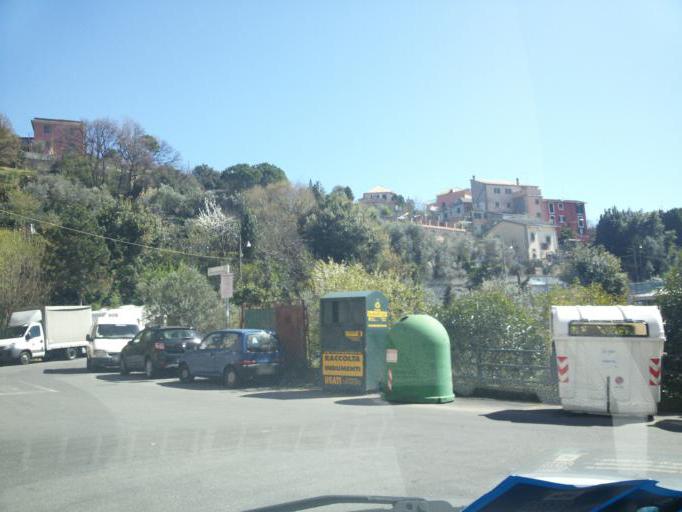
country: IT
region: Liguria
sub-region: Provincia di Genova
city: Genoa
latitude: 44.4154
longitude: 8.9803
